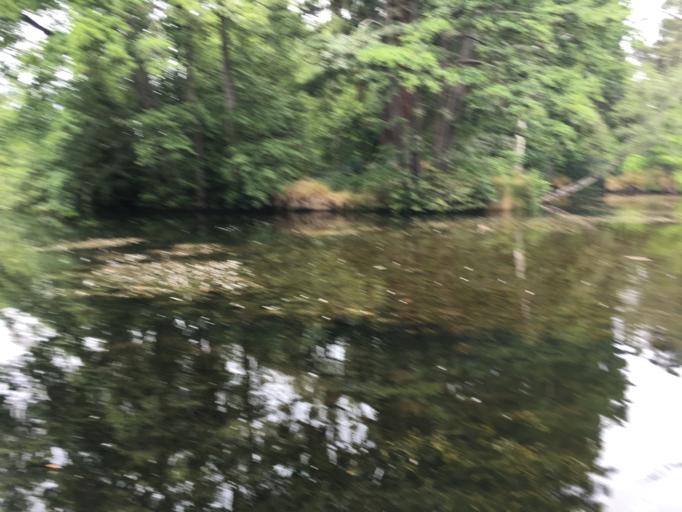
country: NZ
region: Canterbury
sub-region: Christchurch City
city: Christchurch
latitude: -43.5291
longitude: 172.6208
